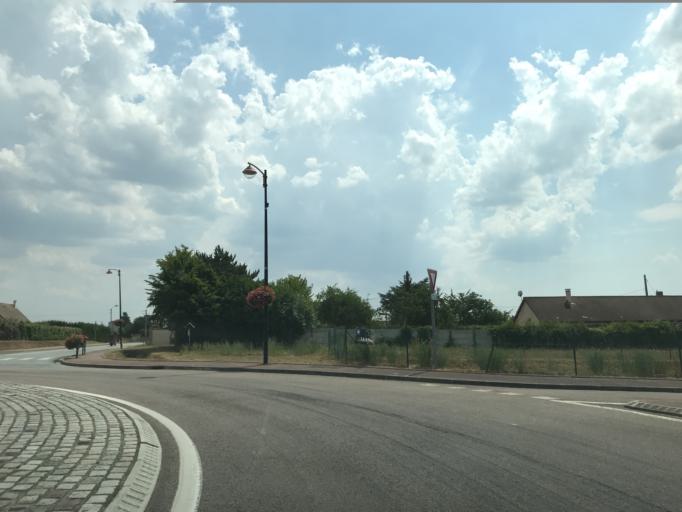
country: FR
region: Haute-Normandie
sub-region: Departement de l'Eure
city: Bueil
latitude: 48.9390
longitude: 1.4361
